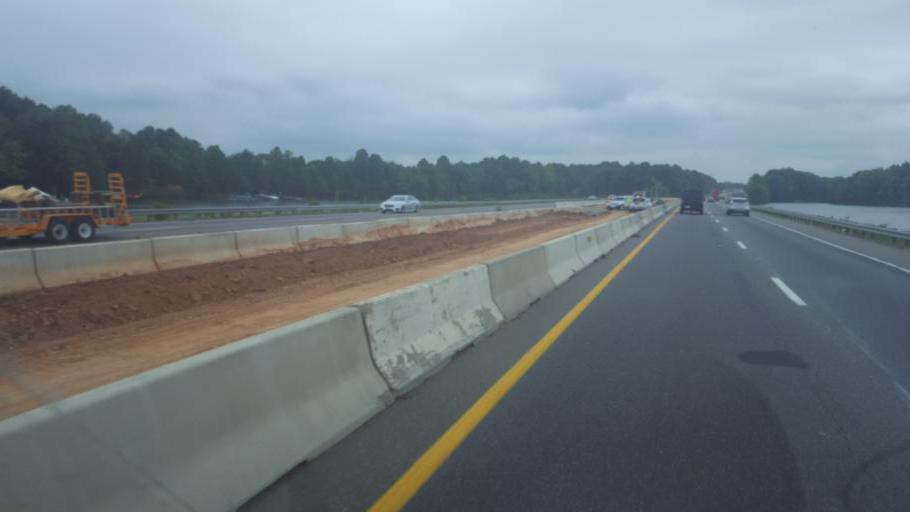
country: US
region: North Carolina
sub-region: Mecklenburg County
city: Cornelius
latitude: 35.5139
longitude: -80.8655
